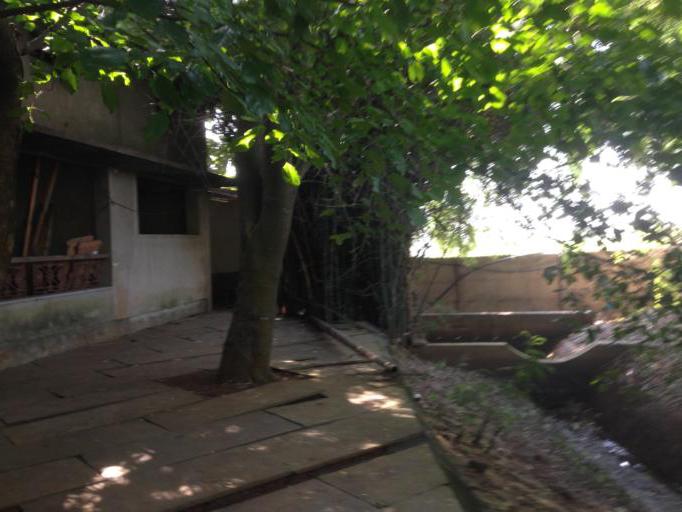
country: IN
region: Karnataka
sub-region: Belgaum
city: Belgaum
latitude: 15.8224
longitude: 74.4817
